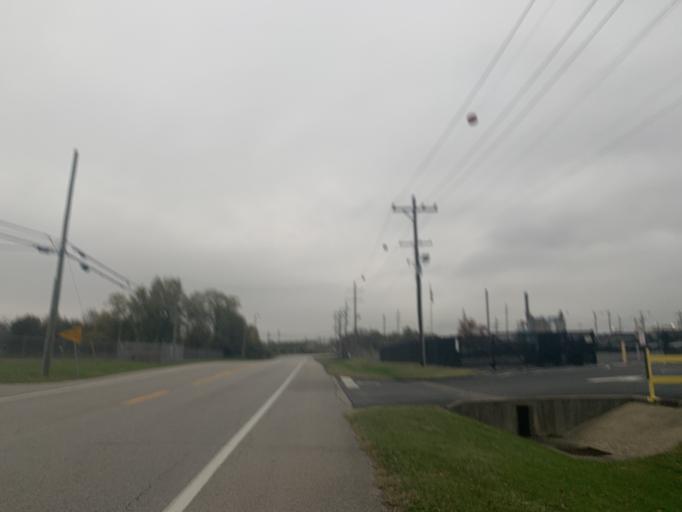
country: US
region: Kentucky
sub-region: Jefferson County
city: Shively
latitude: 38.2101
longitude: -85.8423
